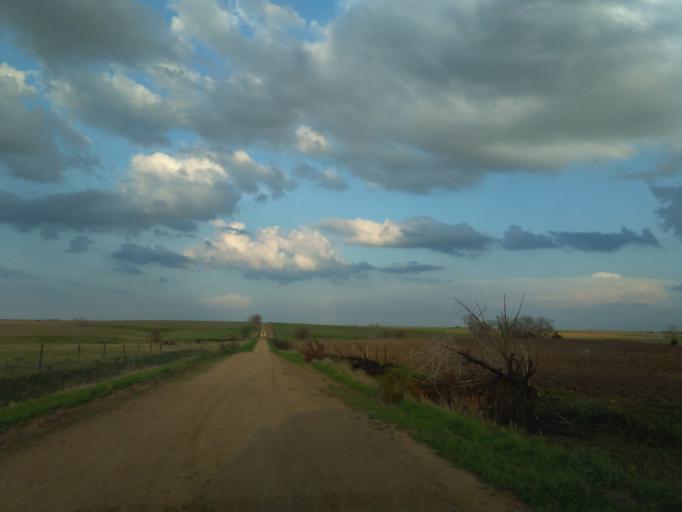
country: US
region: Nebraska
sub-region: Webster County
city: Red Cloud
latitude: 40.2054
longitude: -98.3728
